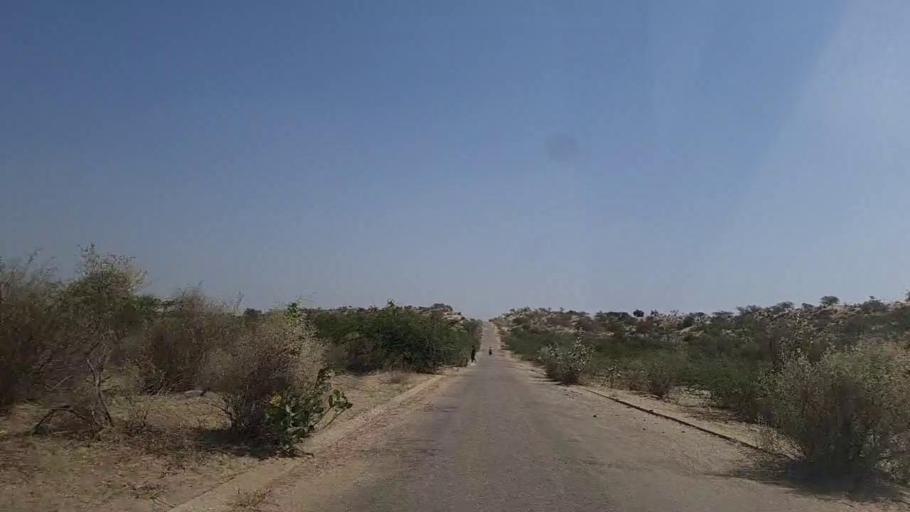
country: PK
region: Sindh
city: Diplo
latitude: 24.5136
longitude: 69.4048
